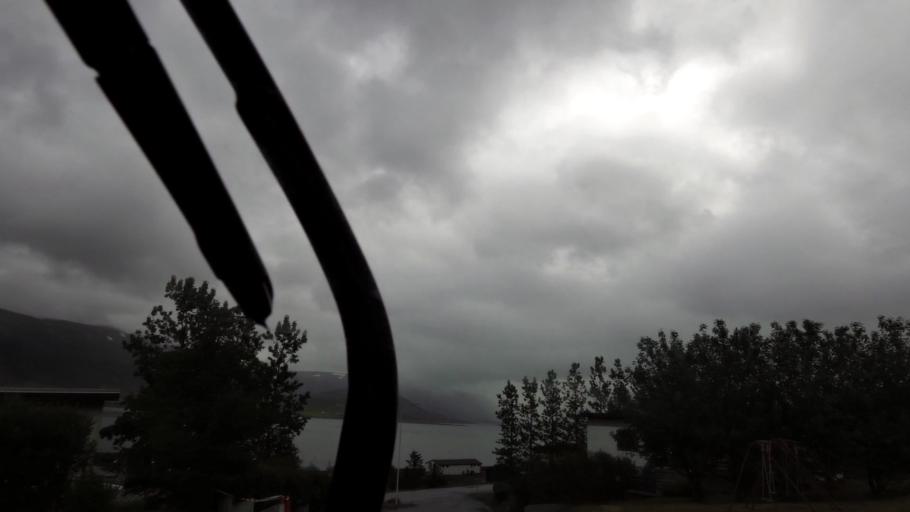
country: IS
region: Westfjords
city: Isafjoerdur
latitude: 65.8756
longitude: -23.4915
